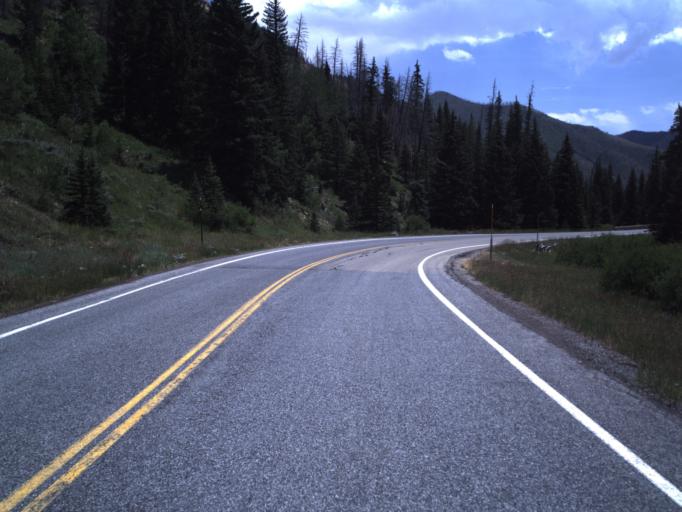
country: US
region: Utah
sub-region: Sanpete County
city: Fairview
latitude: 39.5506
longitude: -111.1686
